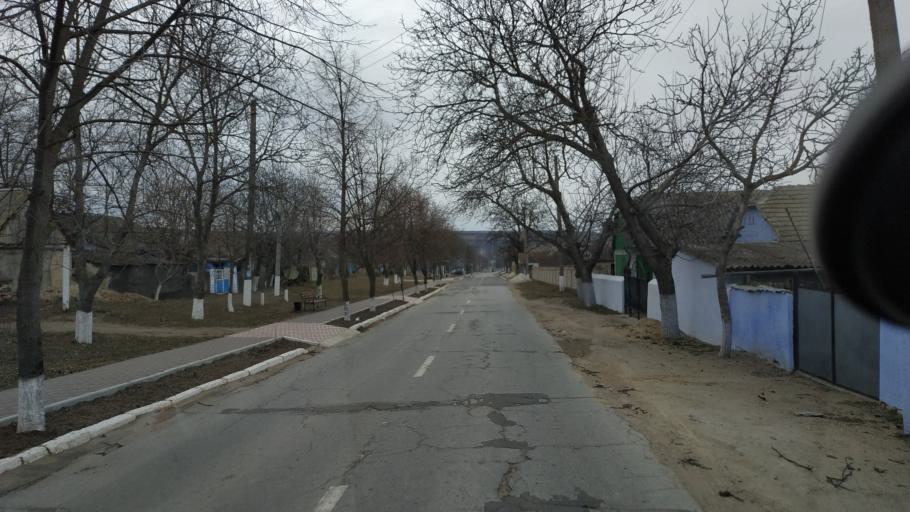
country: MD
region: Telenesti
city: Cocieri
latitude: 47.3426
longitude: 29.0945
